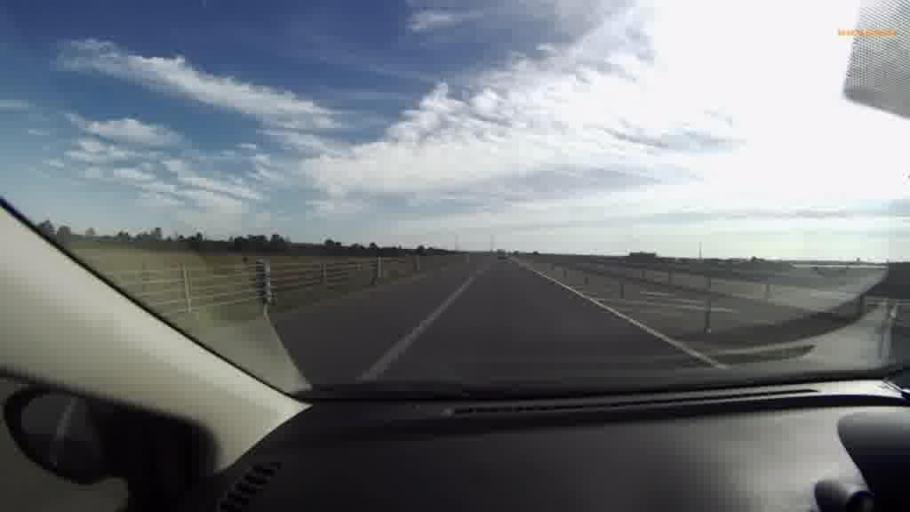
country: JP
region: Hokkaido
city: Kushiro
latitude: 43.0373
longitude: 144.3453
